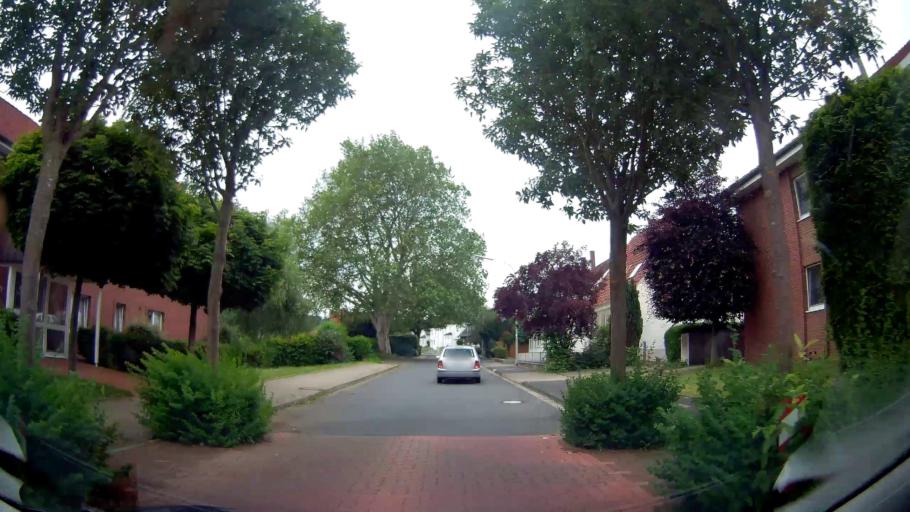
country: DE
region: North Rhine-Westphalia
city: Loehne
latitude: 52.1937
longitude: 8.7194
